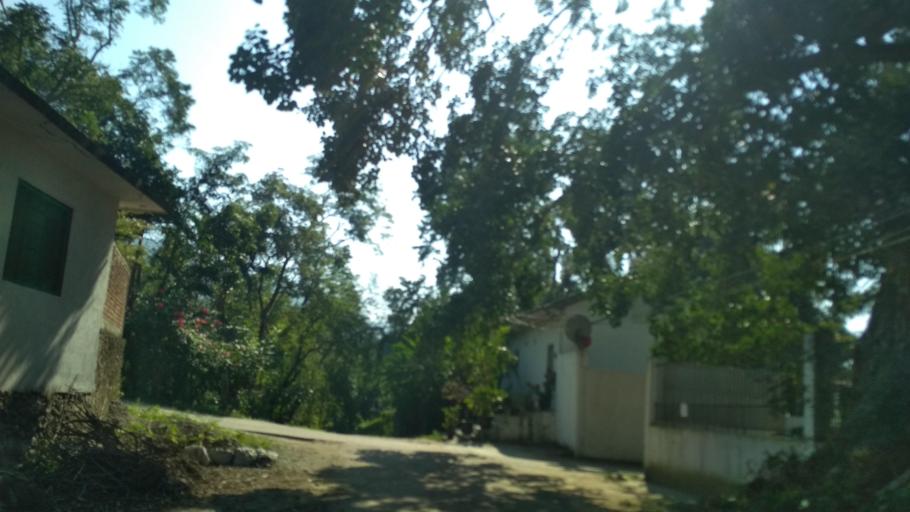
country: MX
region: Veracruz
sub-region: Papantla
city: Polutla
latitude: 20.4623
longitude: -97.1933
